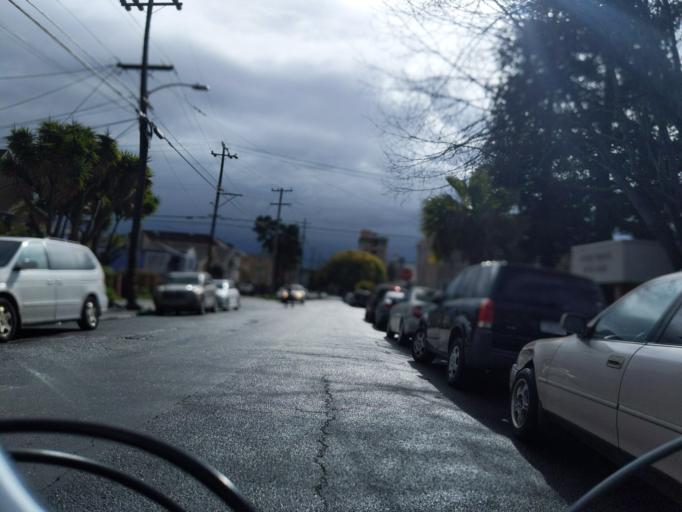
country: US
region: California
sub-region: Alameda County
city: Alameda
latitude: 37.7828
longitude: -122.2296
